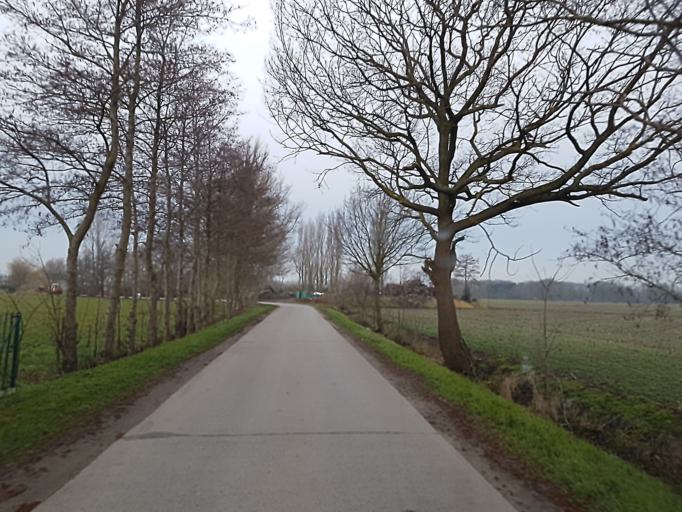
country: BE
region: Flanders
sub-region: Provincie Oost-Vlaanderen
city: Assenede
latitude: 51.1967
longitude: 3.7254
